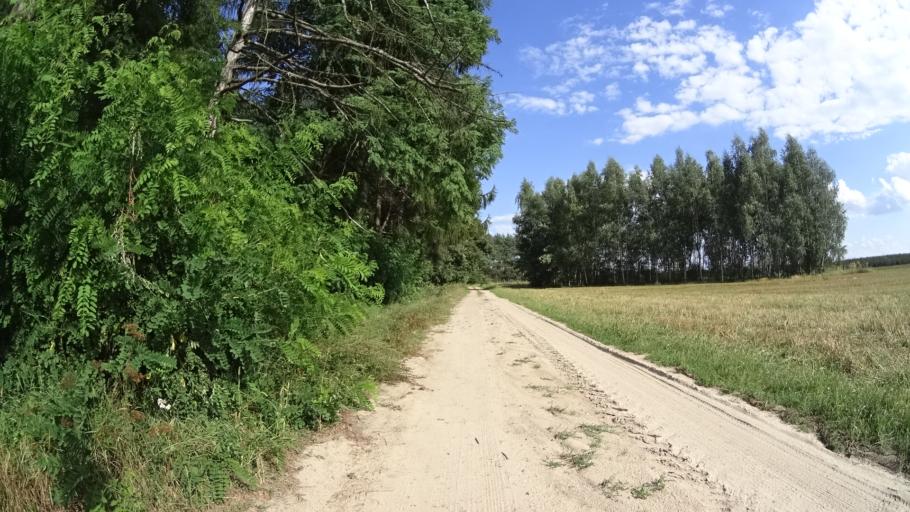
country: PL
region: Masovian Voivodeship
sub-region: Powiat bialobrzeski
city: Wysmierzyce
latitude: 51.6764
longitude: 20.7810
